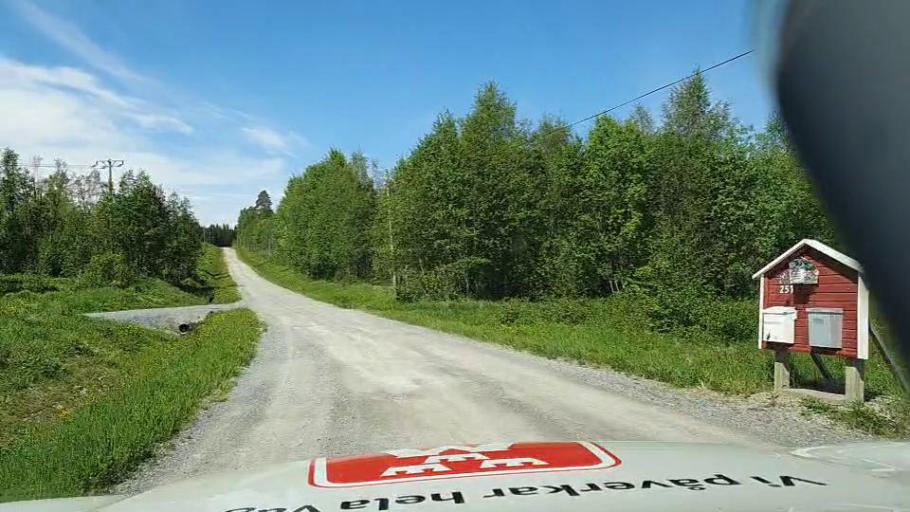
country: SE
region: Jaemtland
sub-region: Bergs Kommun
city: Hoverberg
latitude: 62.8726
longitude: 14.6207
